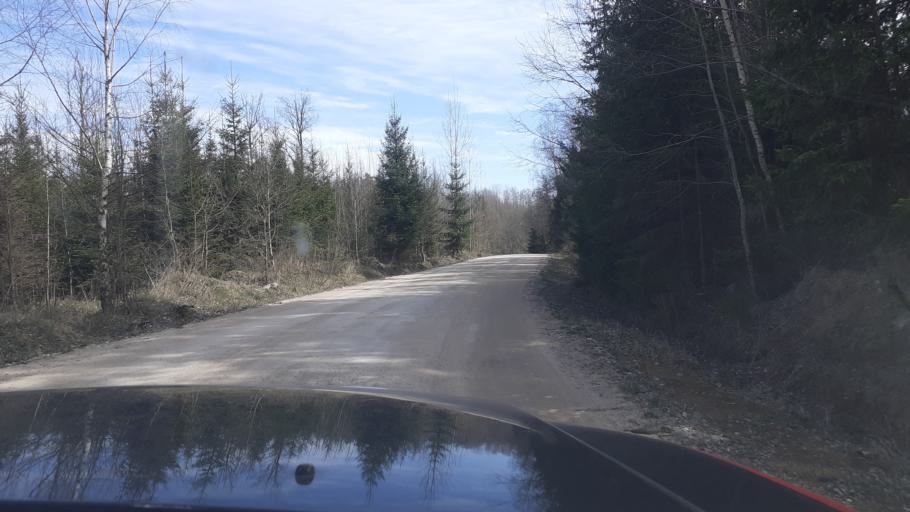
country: LV
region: Kuldigas Rajons
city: Kuldiga
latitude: 56.8458
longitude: 21.9719
